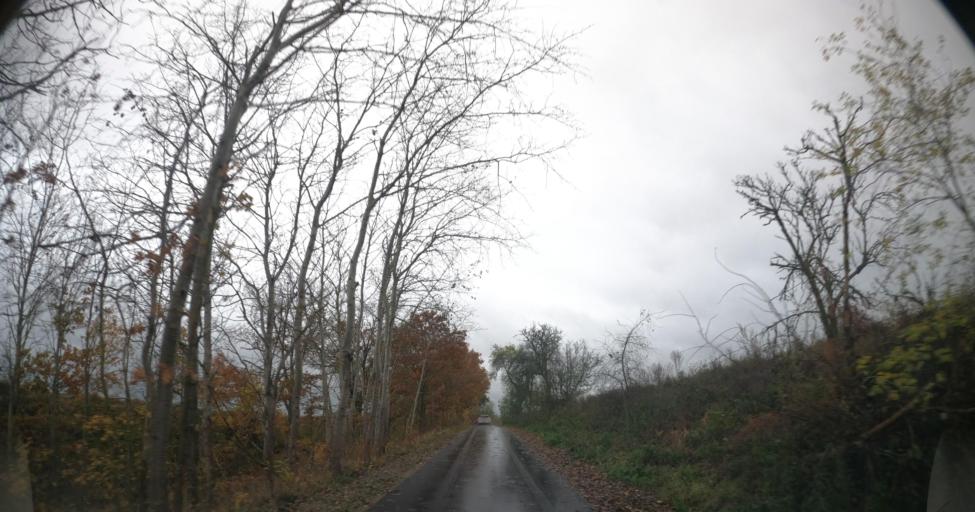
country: PL
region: West Pomeranian Voivodeship
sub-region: Powiat policki
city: Kolbaskowo
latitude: 53.3631
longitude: 14.3605
